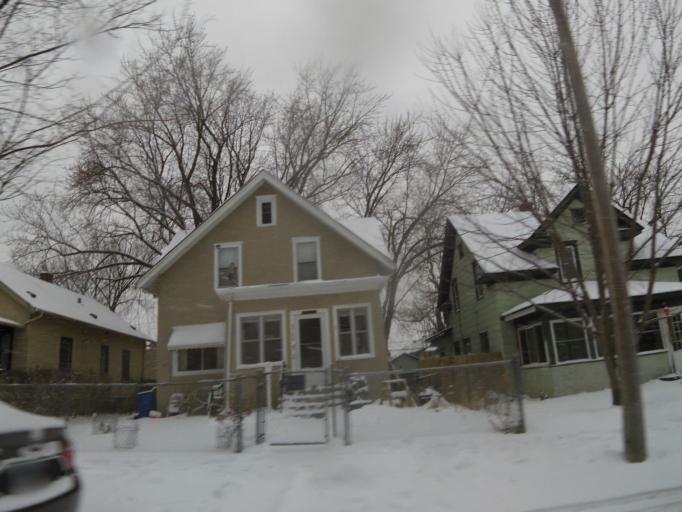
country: US
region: Minnesota
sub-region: Hennepin County
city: Minneapolis
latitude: 44.9354
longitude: -93.2613
